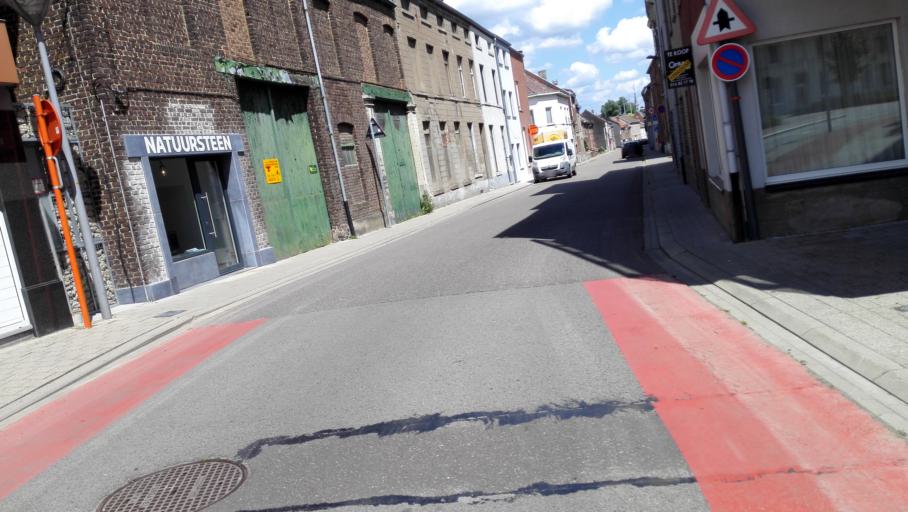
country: BE
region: Flanders
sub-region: Provincie Vlaams-Brabant
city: Tienen
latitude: 50.8011
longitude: 4.9270
